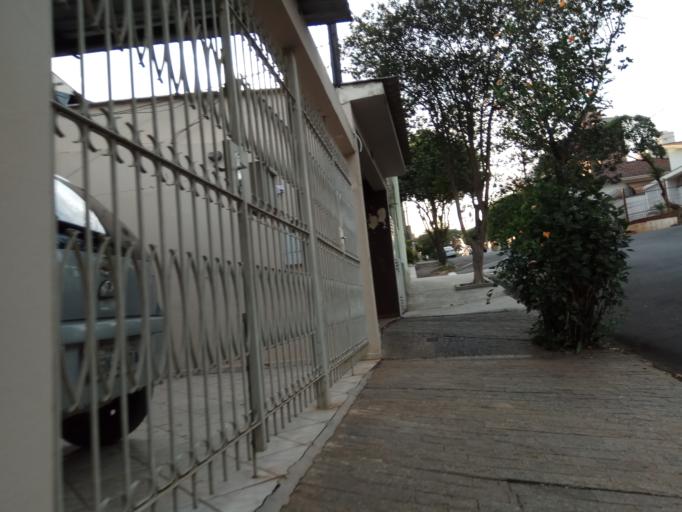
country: BR
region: Sao Paulo
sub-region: Piracicaba
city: Piracicaba
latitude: -22.7098
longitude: -47.6432
